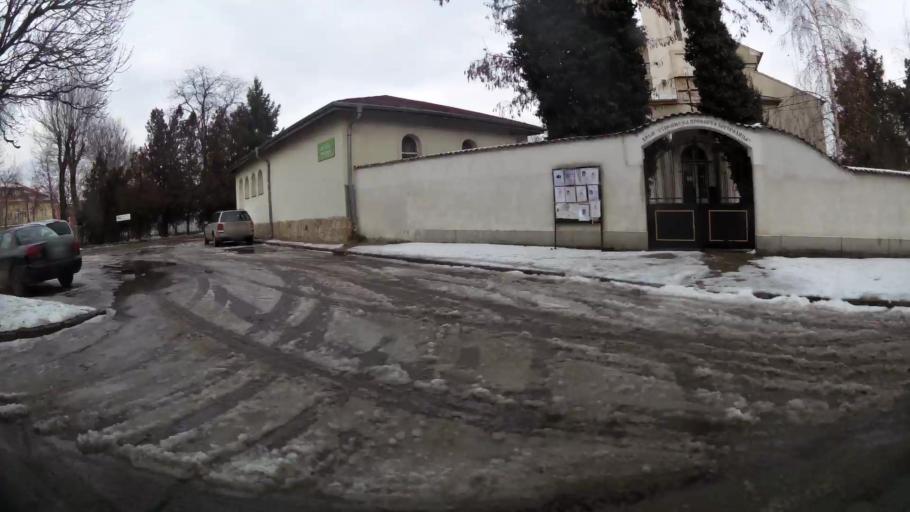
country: BG
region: Sofia-Capital
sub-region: Stolichna Obshtina
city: Sofia
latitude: 42.7178
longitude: 23.3474
